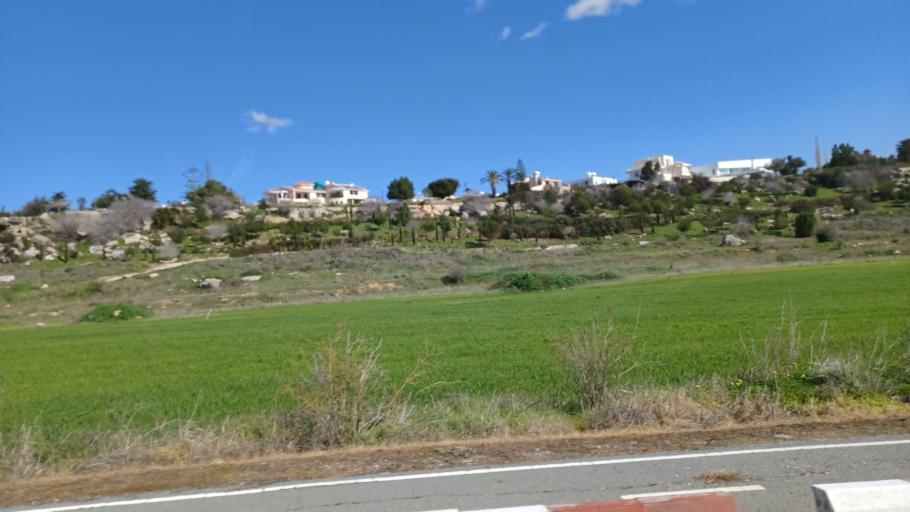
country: CY
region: Pafos
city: Paphos
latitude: 34.7560
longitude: 32.4433
